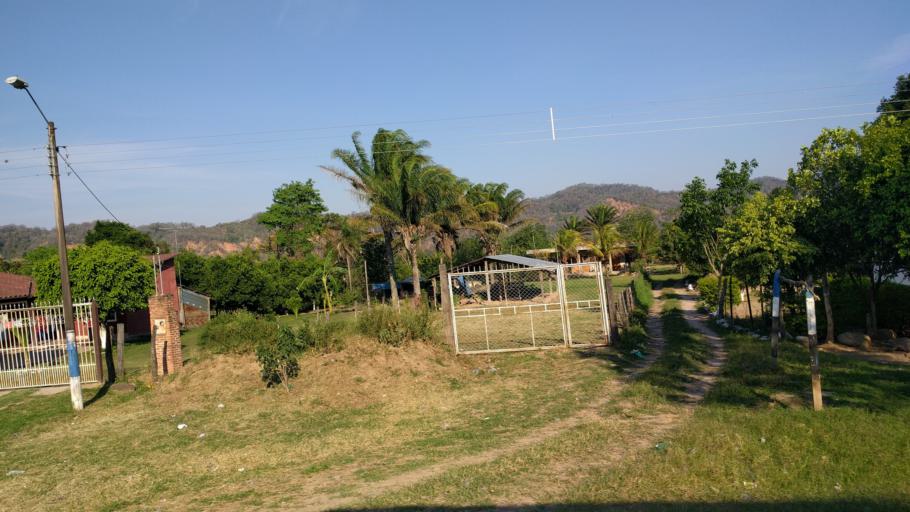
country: BO
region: Santa Cruz
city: Jorochito
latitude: -18.1205
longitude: -63.4628
